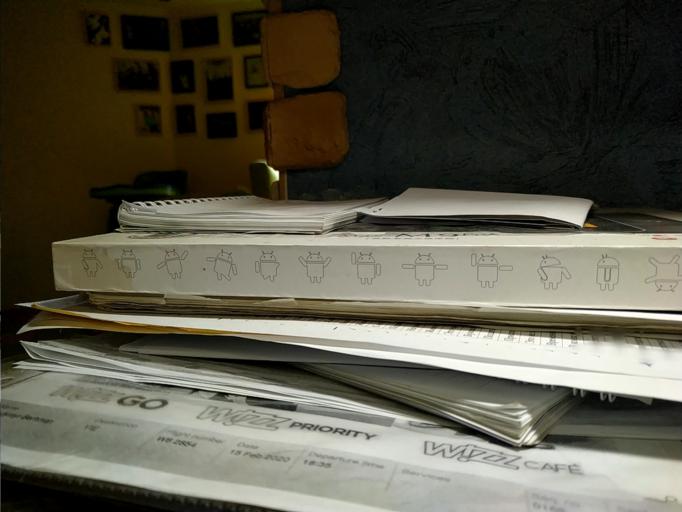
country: RU
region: Novgorod
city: Volot
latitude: 57.7013
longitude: 30.6657
